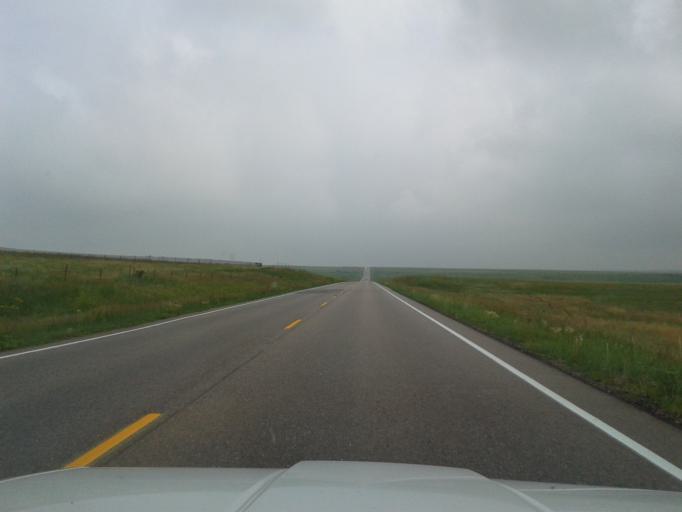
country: US
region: Colorado
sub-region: Elbert County
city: Ponderosa Park
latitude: 39.2917
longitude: -104.7362
